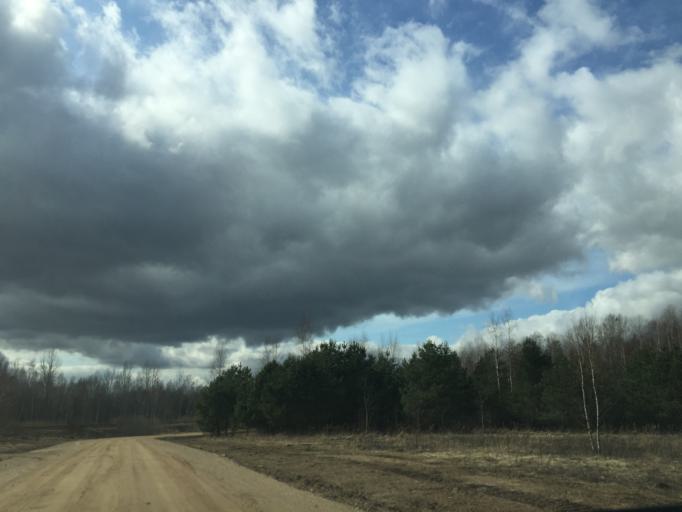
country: LV
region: Vecumnieki
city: Vecumnieki
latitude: 56.5855
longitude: 24.6055
